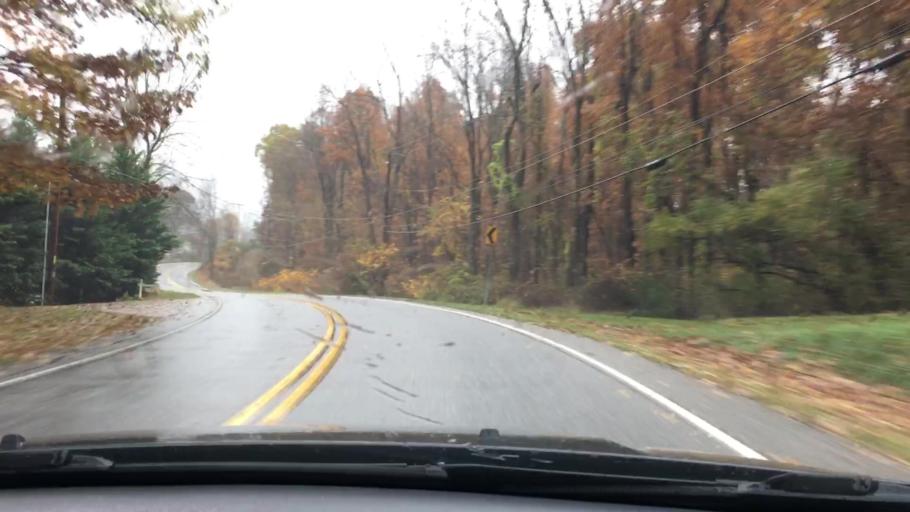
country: US
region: Pennsylvania
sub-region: York County
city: Glen Rock
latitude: 39.7734
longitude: -76.7319
